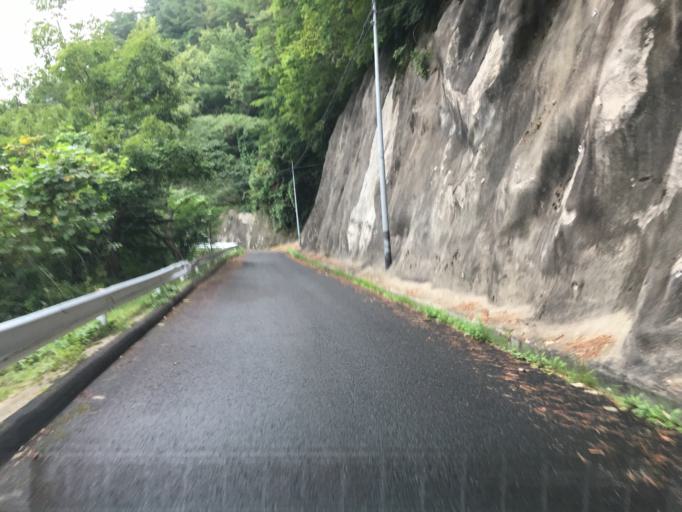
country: JP
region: Fukushima
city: Fukushima-shi
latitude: 37.8089
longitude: 140.3528
